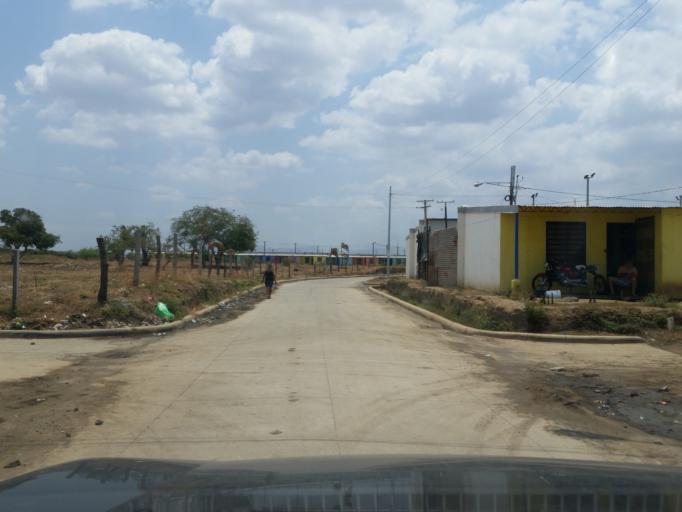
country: NI
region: Managua
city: Tipitapa
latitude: 12.1322
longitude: -86.1566
